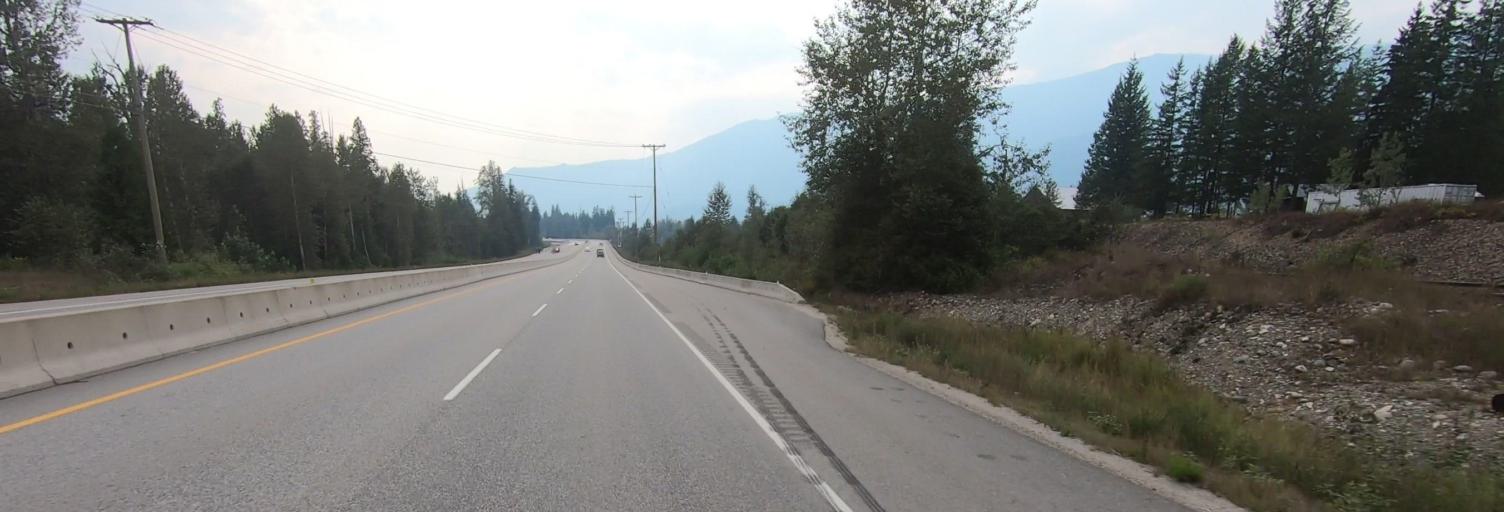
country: CA
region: British Columbia
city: Sicamous
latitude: 50.9499
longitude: -118.7686
